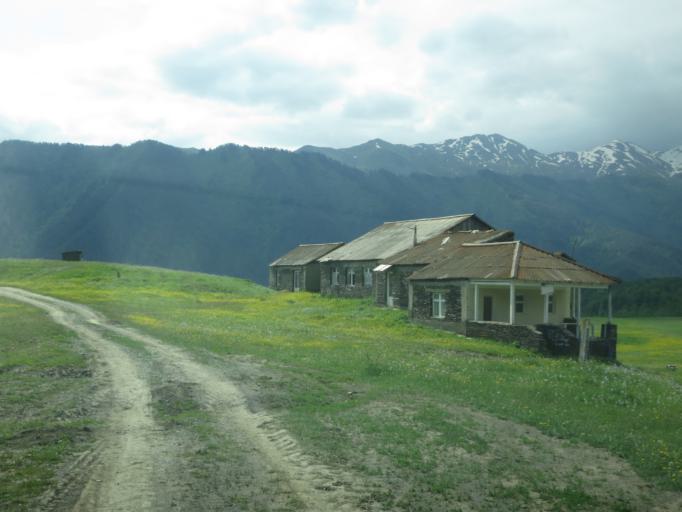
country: RU
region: Chechnya
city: Itum-Kali
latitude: 42.3685
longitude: 45.6366
